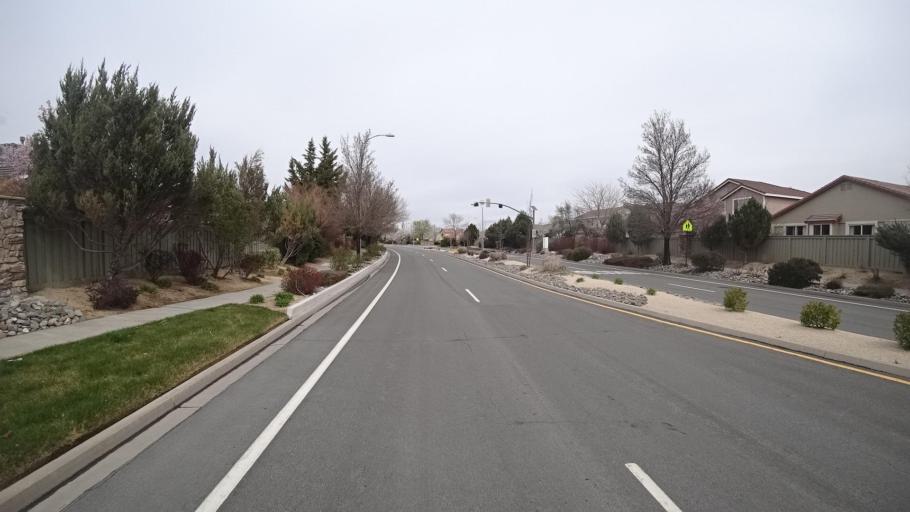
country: US
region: Nevada
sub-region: Washoe County
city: Sparks
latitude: 39.4382
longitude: -119.7419
